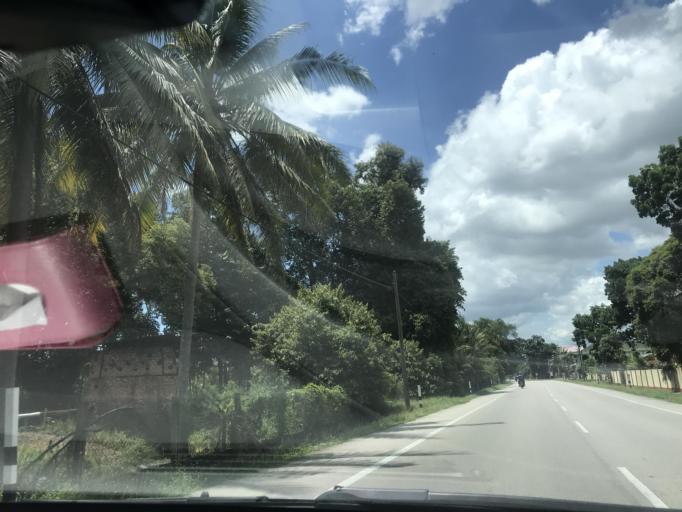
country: MY
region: Kelantan
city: Tumpat
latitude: 6.1802
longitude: 102.1761
